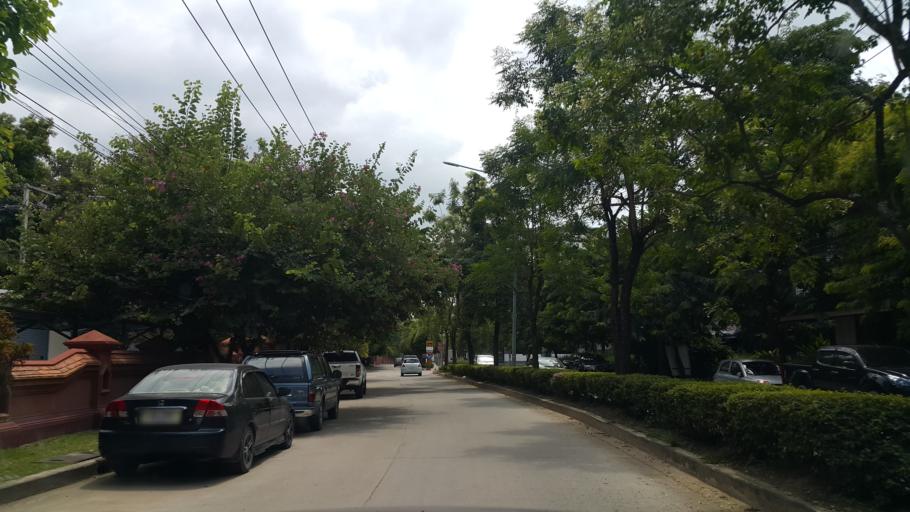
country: TH
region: Chiang Mai
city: Chiang Mai
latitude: 18.8019
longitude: 99.0248
